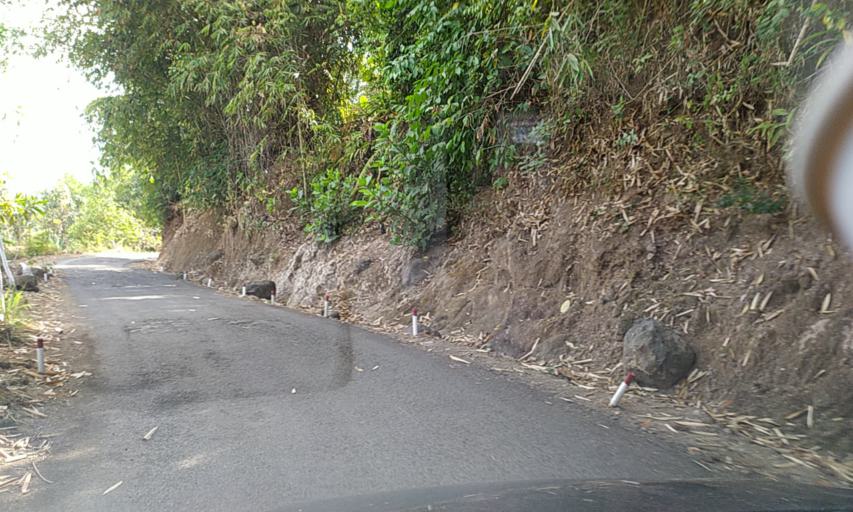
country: ID
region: Central Java
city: Pasirmanggu
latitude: -7.2330
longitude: 108.5914
